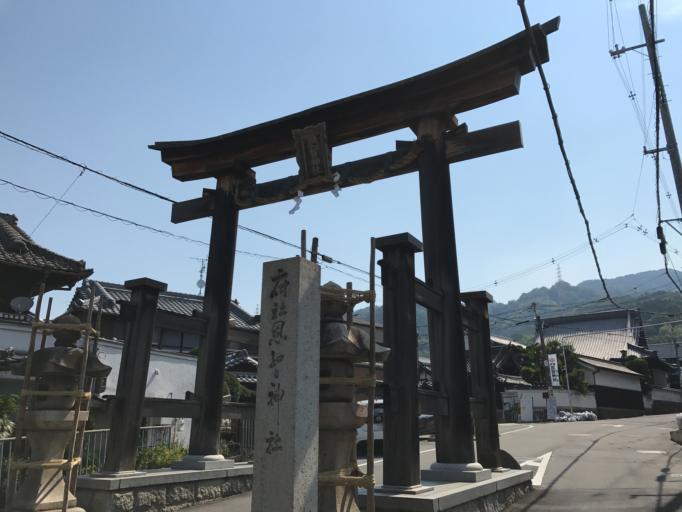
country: JP
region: Osaka
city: Kashihara
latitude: 34.6078
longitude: 135.6324
